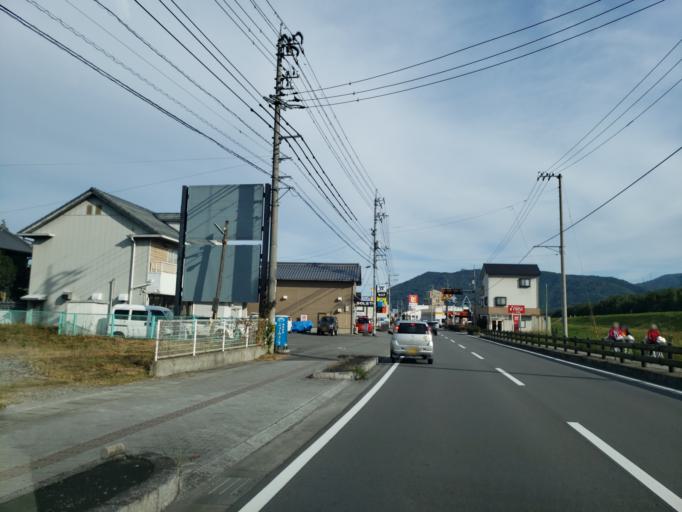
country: JP
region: Tokushima
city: Wakimachi
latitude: 34.0649
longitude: 134.1517
